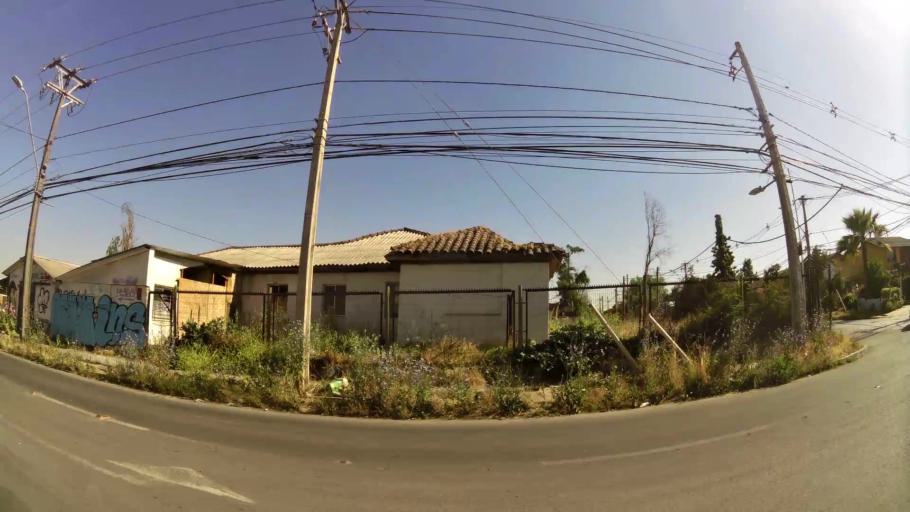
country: CL
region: Santiago Metropolitan
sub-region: Provincia de Maipo
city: San Bernardo
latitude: -33.5670
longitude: -70.7072
